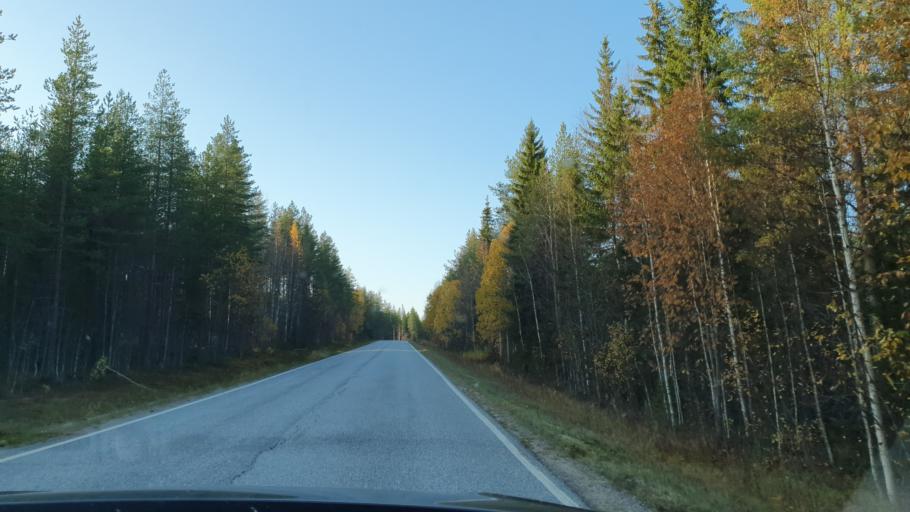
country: FI
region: Kainuu
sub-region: Kehys-Kainuu
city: Kuhmo
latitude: 64.3770
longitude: 29.4814
